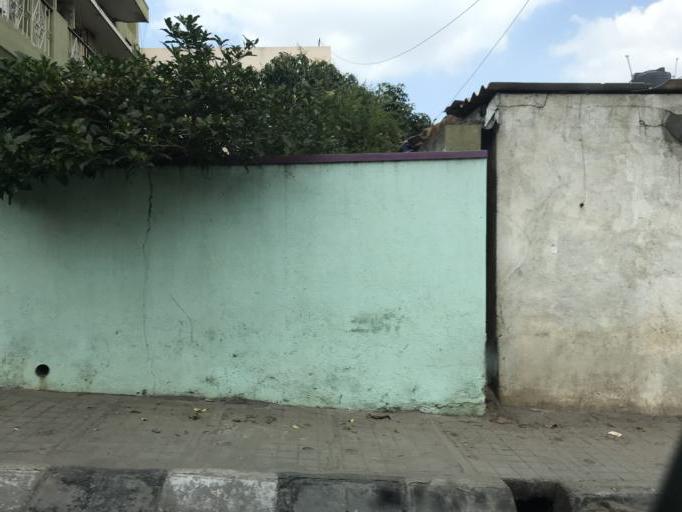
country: IN
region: Karnataka
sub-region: Bangalore Urban
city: Bangalore
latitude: 13.0005
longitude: 77.5259
